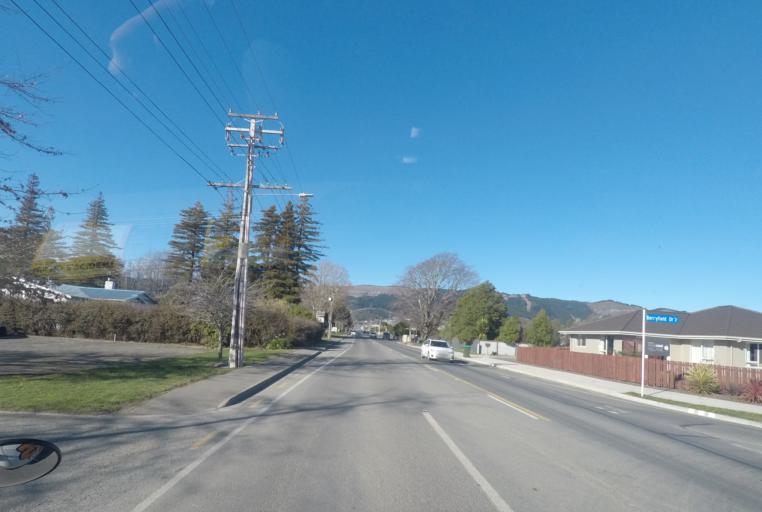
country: NZ
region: Tasman
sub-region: Tasman District
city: Richmond
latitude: -41.3318
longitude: 173.1765
